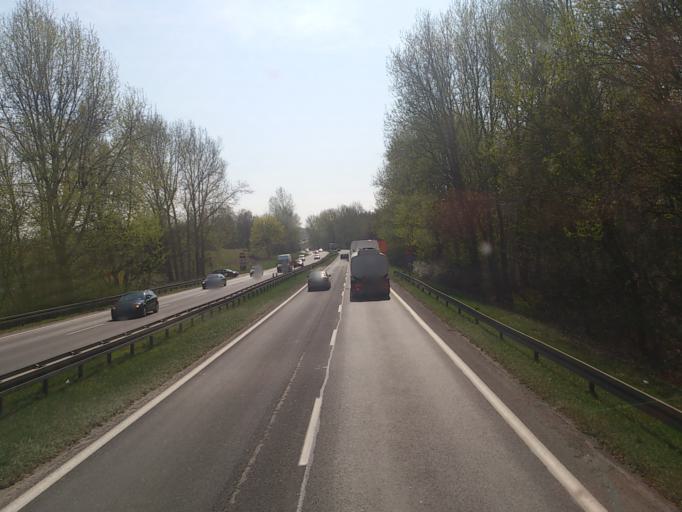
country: PL
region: Silesian Voivodeship
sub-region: Powiat bedzinski
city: Siewierz
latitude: 50.4502
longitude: 19.2268
